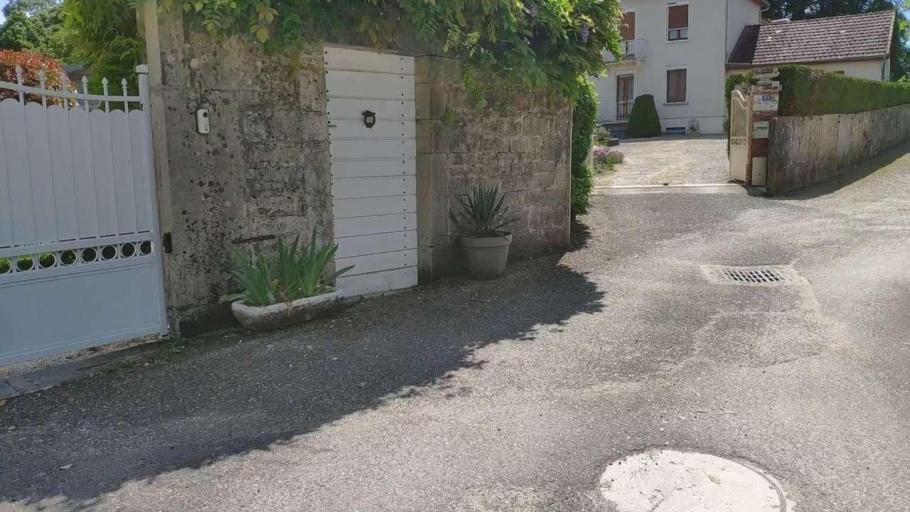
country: FR
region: Franche-Comte
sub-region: Departement du Jura
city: Bletterans
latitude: 46.7441
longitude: 5.4955
